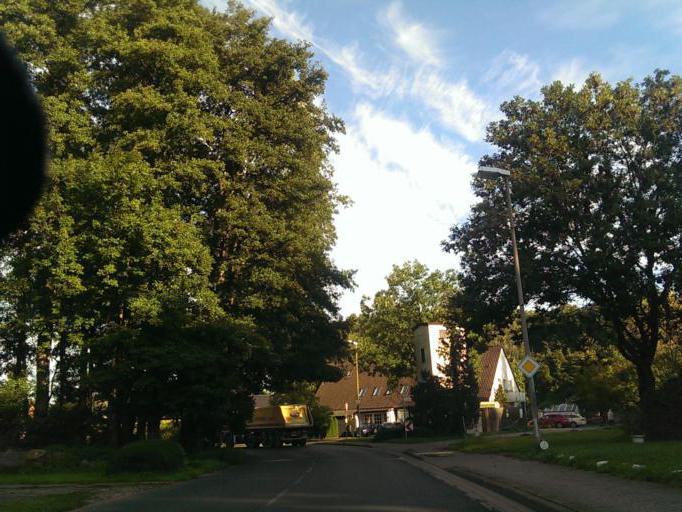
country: DE
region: Lower Saxony
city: Lindwedel
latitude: 52.5526
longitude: 9.6366
